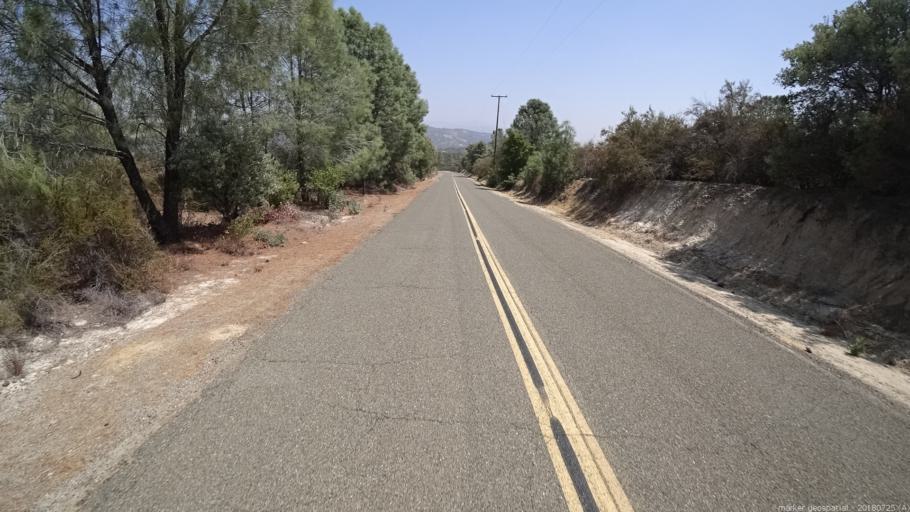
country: US
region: California
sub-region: San Luis Obispo County
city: San Miguel
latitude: 35.9205
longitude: -120.5202
